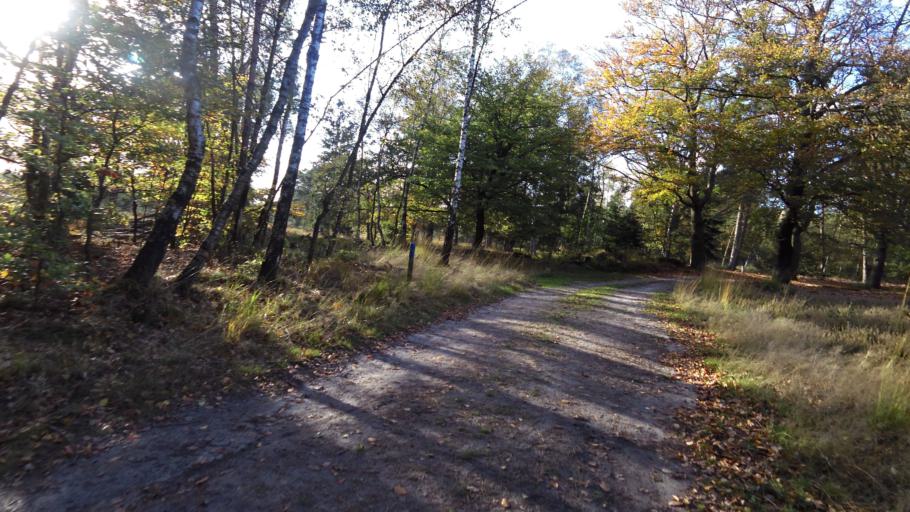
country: NL
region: Gelderland
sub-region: Gemeente Epe
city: Epe
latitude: 52.3897
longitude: 5.9621
